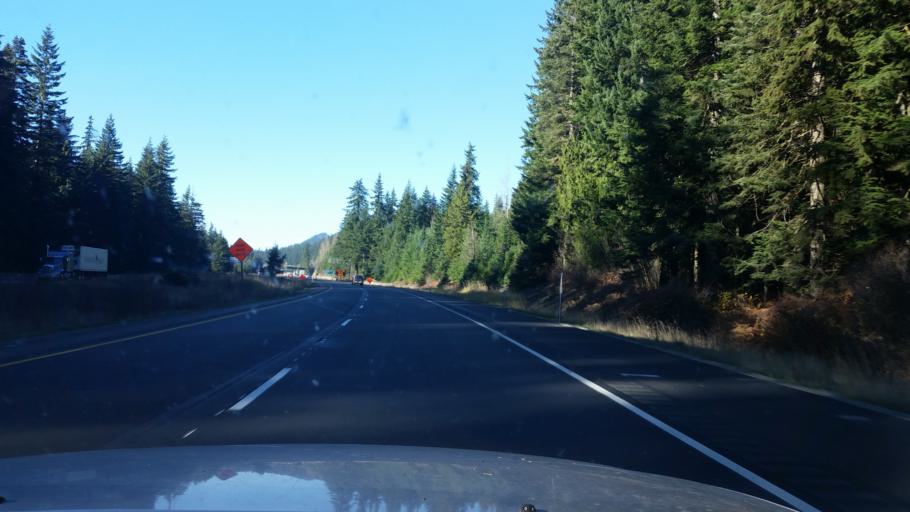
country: US
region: Washington
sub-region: Kittitas County
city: Cle Elum
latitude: 47.3130
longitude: -121.3140
